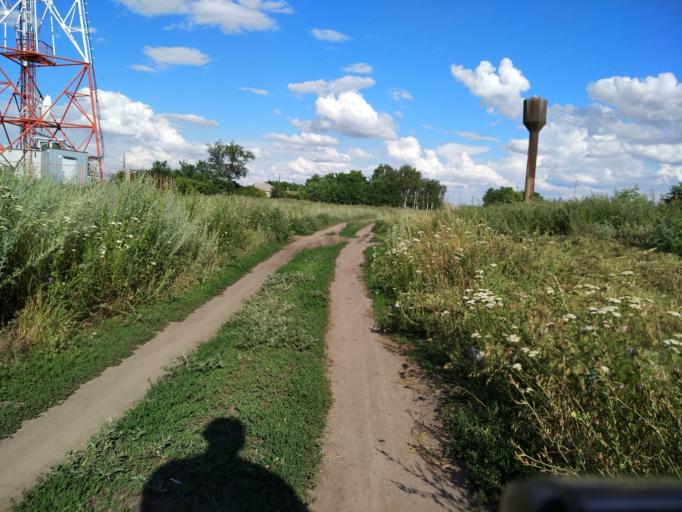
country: RU
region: Lipetsk
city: Dobrinka
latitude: 52.0362
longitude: 40.5559
